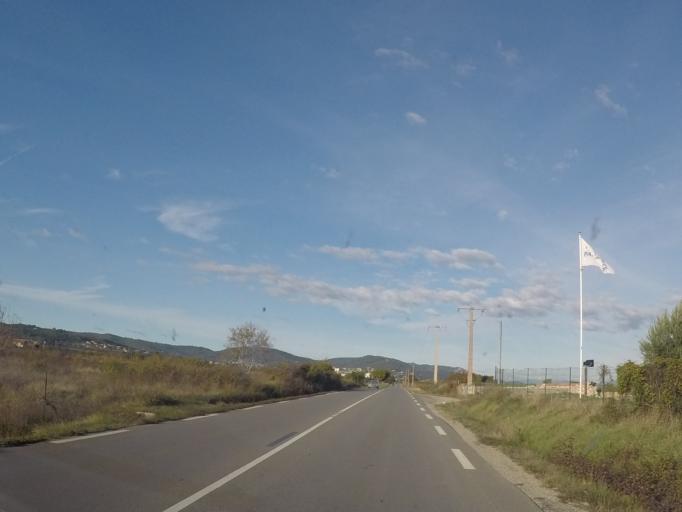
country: FR
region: Provence-Alpes-Cote d'Azur
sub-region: Departement des Alpes-de-Haute-Provence
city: Sainte-Tulle
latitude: 43.7975
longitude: 5.7762
